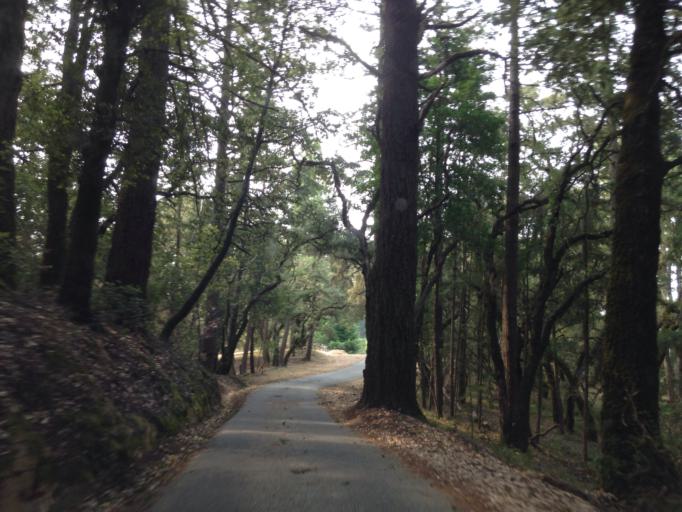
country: US
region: California
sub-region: San Mateo County
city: Portola Valley
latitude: 37.3813
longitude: -122.2961
